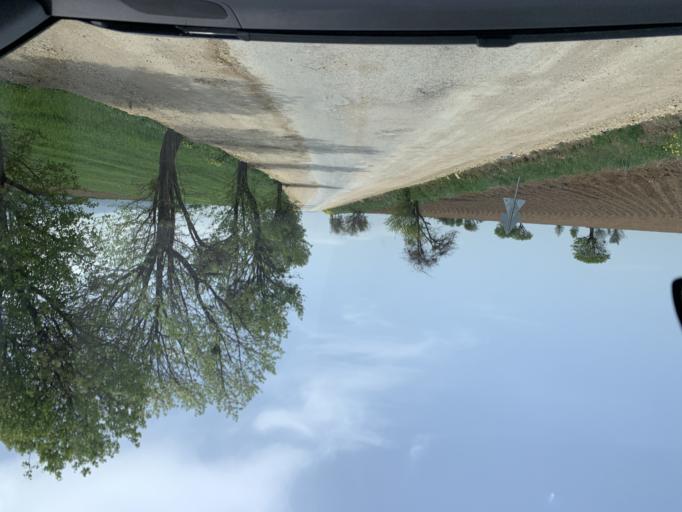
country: TR
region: Bolu
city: Bolu
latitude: 40.7583
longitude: 31.6835
